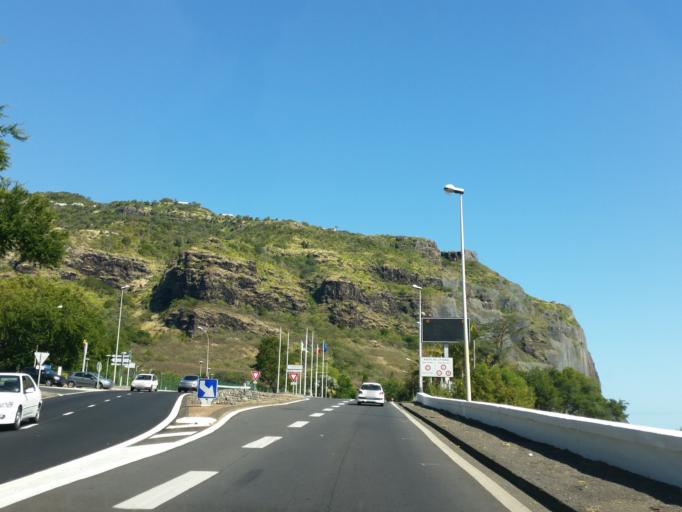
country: RE
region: Reunion
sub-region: Reunion
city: Saint-Denis
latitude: -20.8765
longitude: 55.4429
